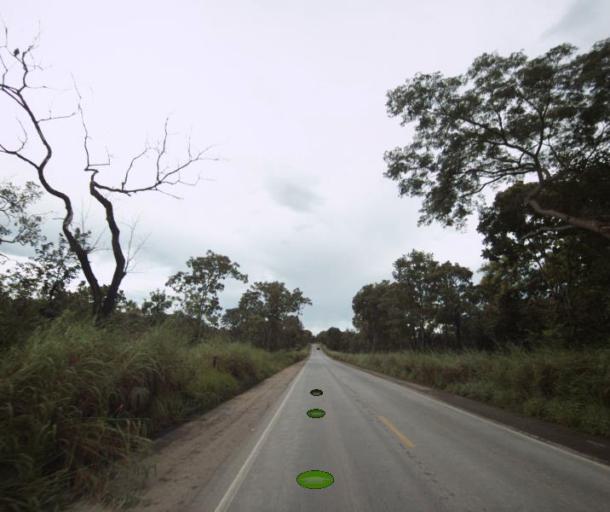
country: BR
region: Goias
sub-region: Porangatu
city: Porangatu
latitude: -13.6228
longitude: -49.0426
